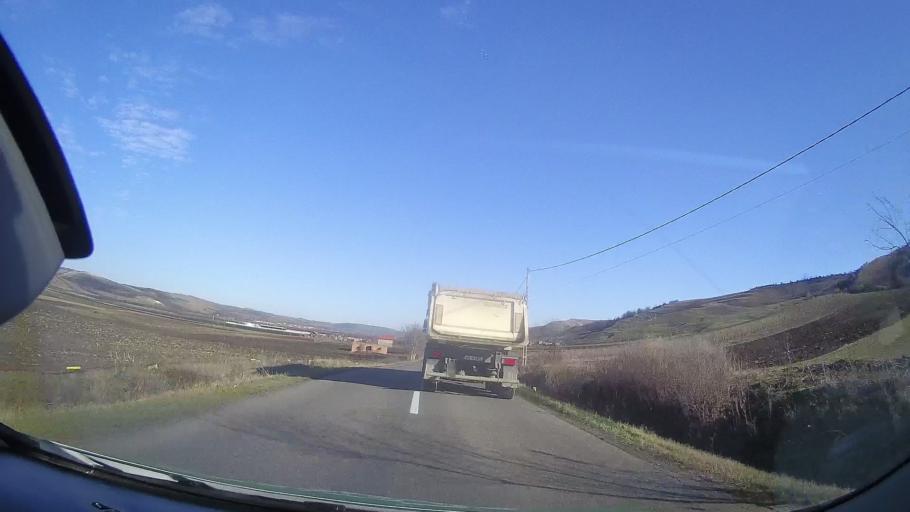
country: RO
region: Mures
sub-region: Comuna Iclanzel
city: Iclanzel
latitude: 46.5442
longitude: 24.3219
